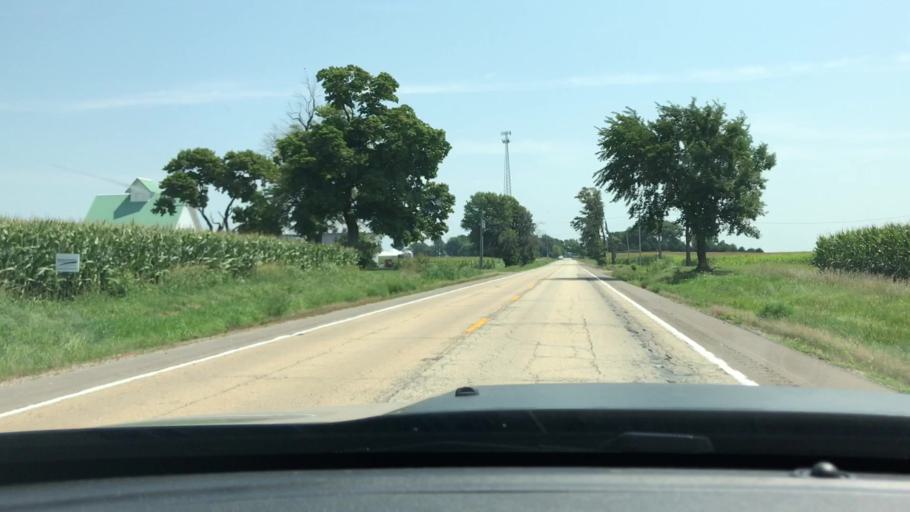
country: US
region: Illinois
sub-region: LaSalle County
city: Earlville
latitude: 41.4690
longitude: -88.9430
